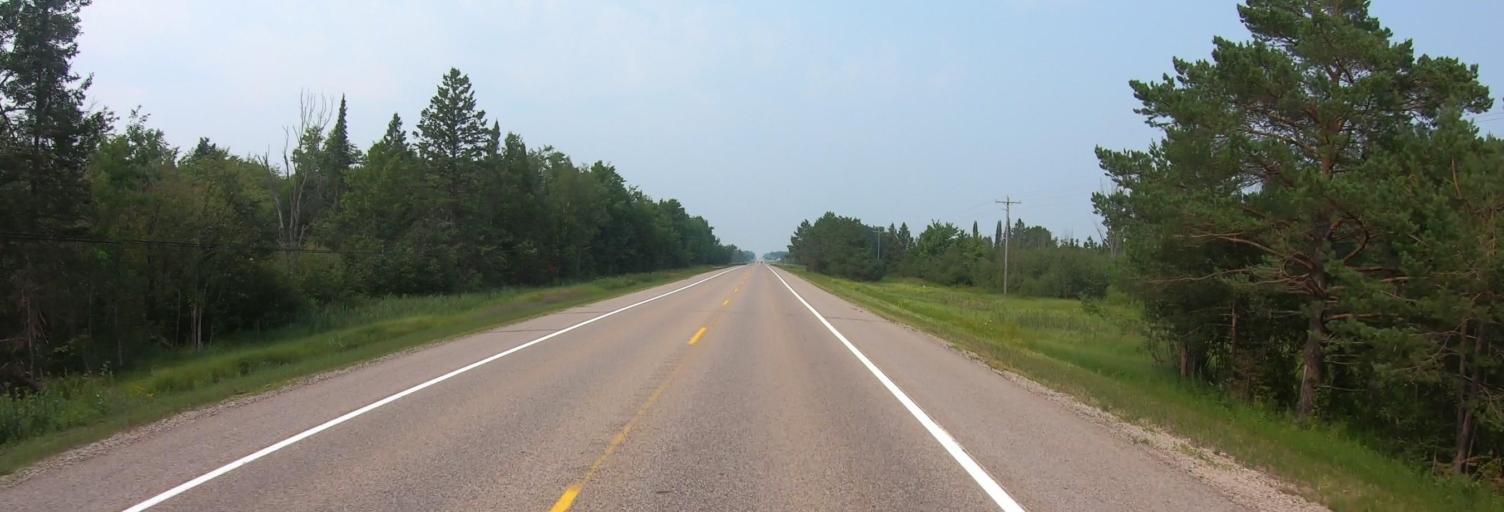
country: US
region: Michigan
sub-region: Chippewa County
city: Sault Ste. Marie
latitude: 46.2692
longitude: -84.3635
